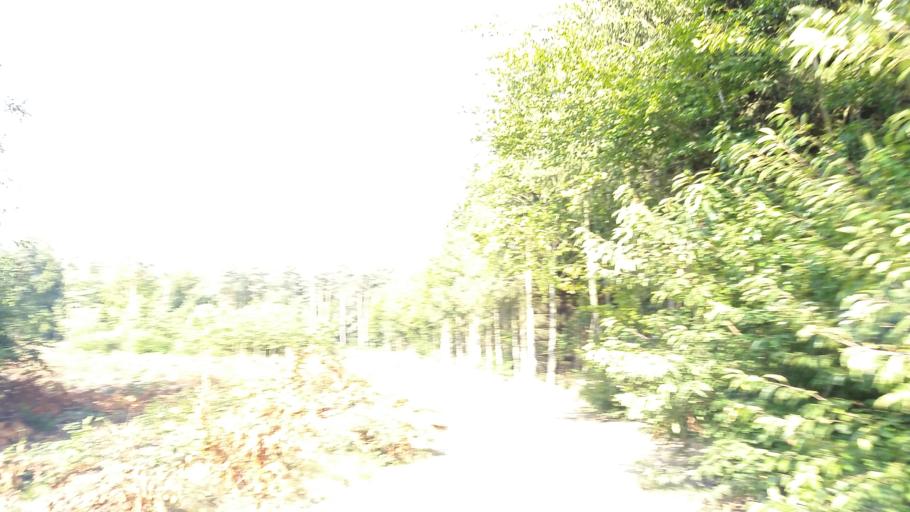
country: PL
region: West Pomeranian Voivodeship
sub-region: Powiat choszczenski
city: Choszczno
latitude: 53.2401
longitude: 15.4236
